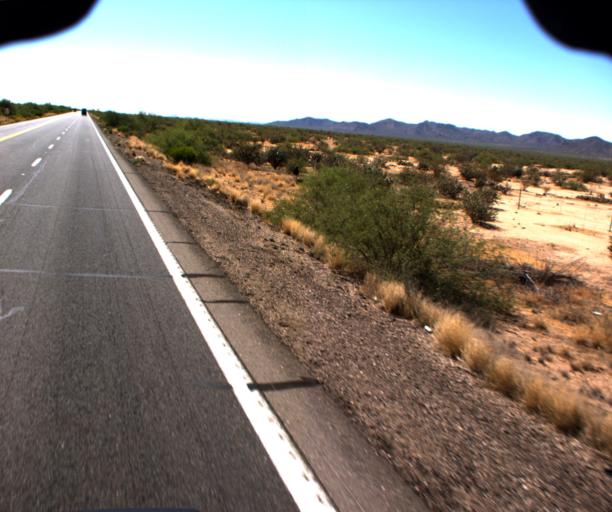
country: US
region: Arizona
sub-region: Yavapai County
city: Congress
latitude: 34.1486
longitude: -112.9869
